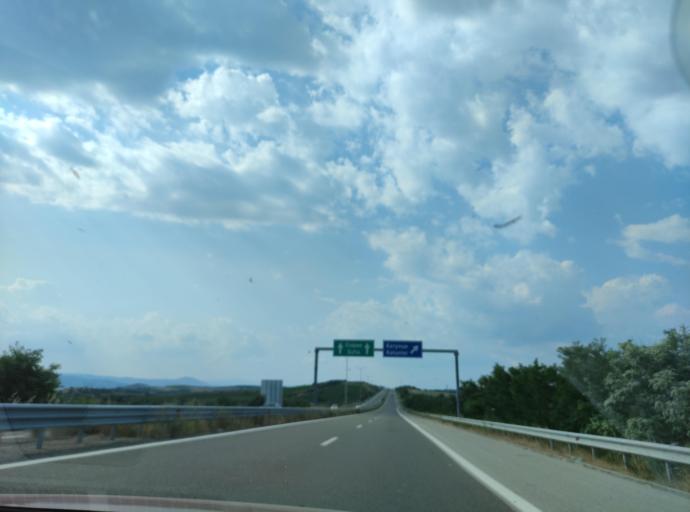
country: BG
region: Blagoevgrad
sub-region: Obshtina Petrich
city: Petrich
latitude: 41.4511
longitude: 23.3232
